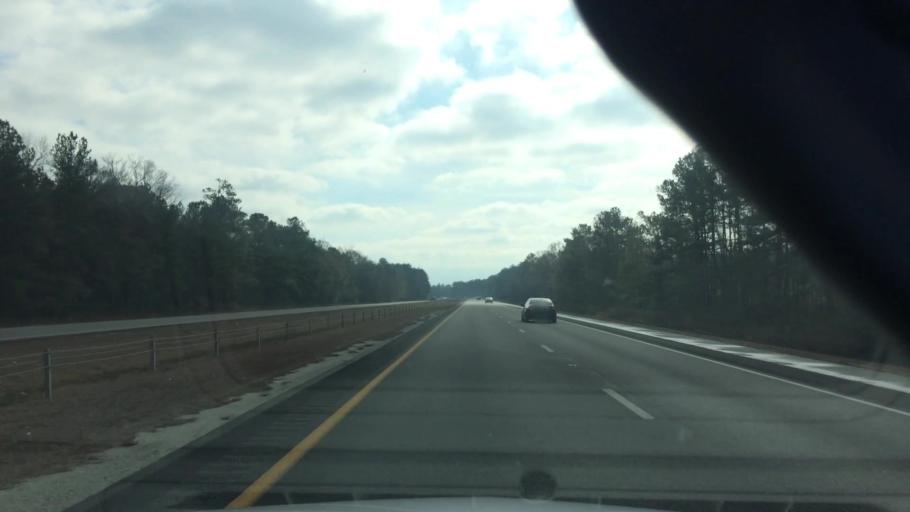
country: US
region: North Carolina
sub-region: Pender County
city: Burgaw
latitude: 34.5445
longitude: -77.8934
